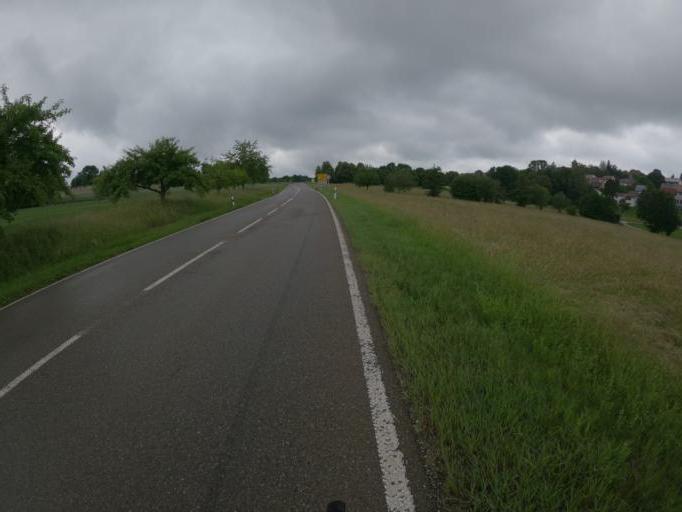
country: DE
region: Baden-Wuerttemberg
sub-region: Regierungsbezirk Stuttgart
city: Adelberg
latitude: 48.7578
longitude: 9.6013
